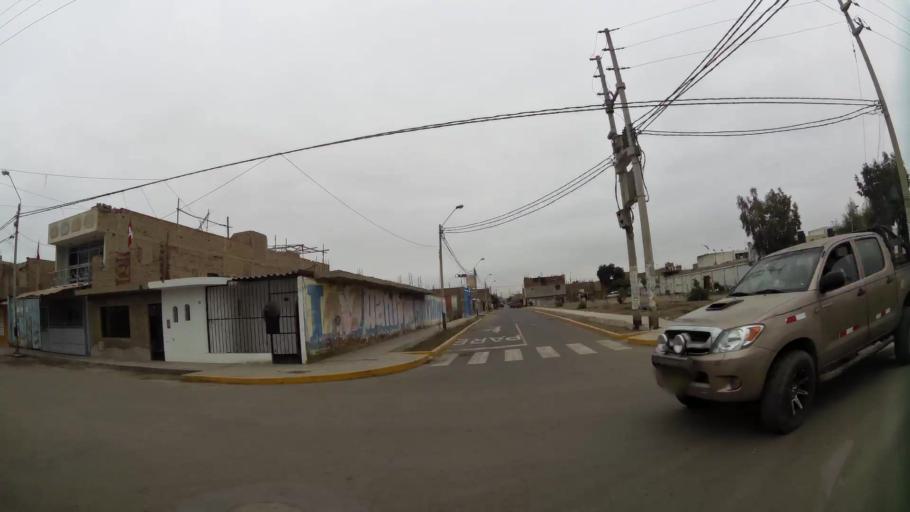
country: PE
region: Ica
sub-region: Provincia de Pisco
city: Pisco
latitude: -13.7192
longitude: -76.2042
